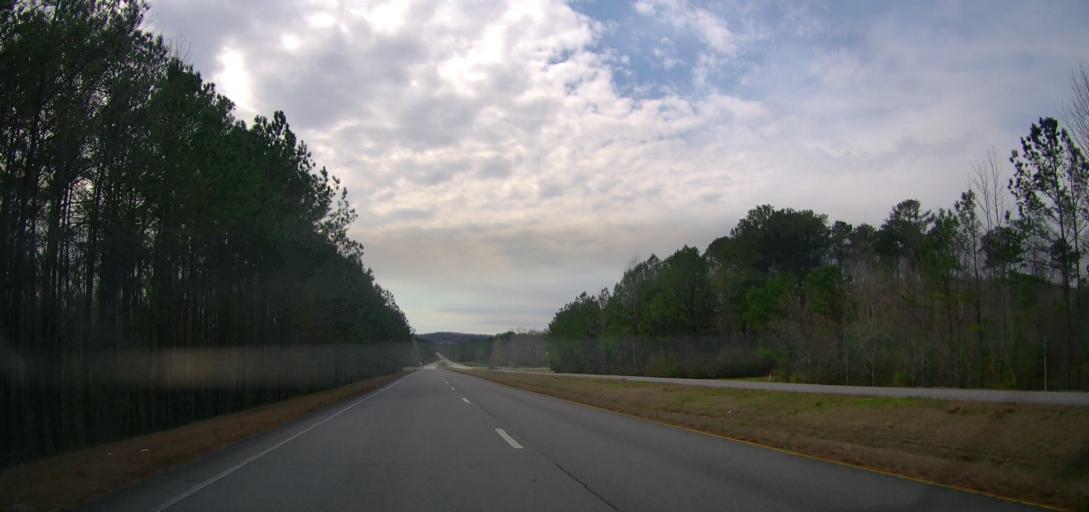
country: US
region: Alabama
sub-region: Marion County
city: Winfield
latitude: 33.9323
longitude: -87.7013
